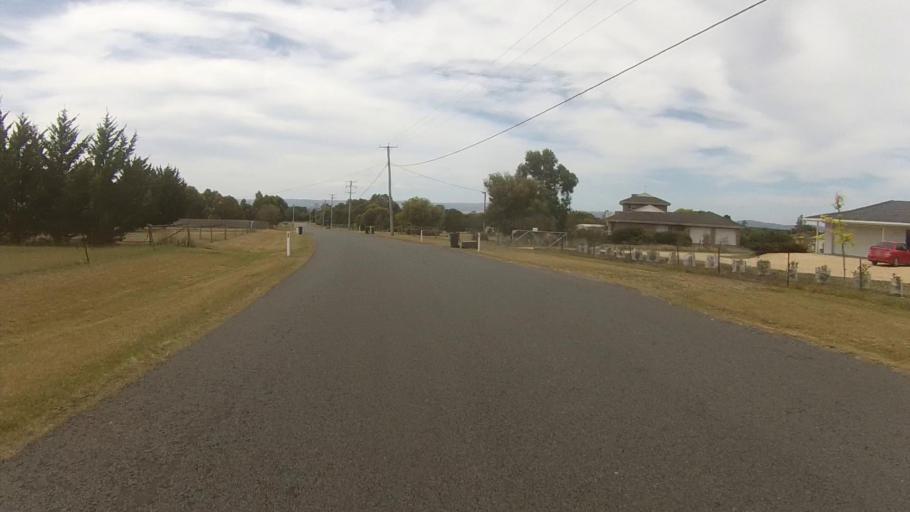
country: AU
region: Tasmania
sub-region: Clarence
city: Cambridge
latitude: -42.8465
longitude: 147.4718
